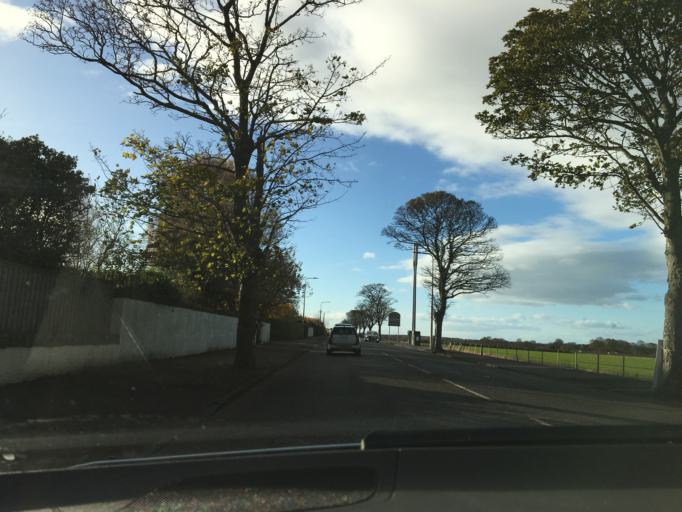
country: GB
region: Scotland
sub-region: East Lothian
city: North Berwick
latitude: 56.0561
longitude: -2.7441
